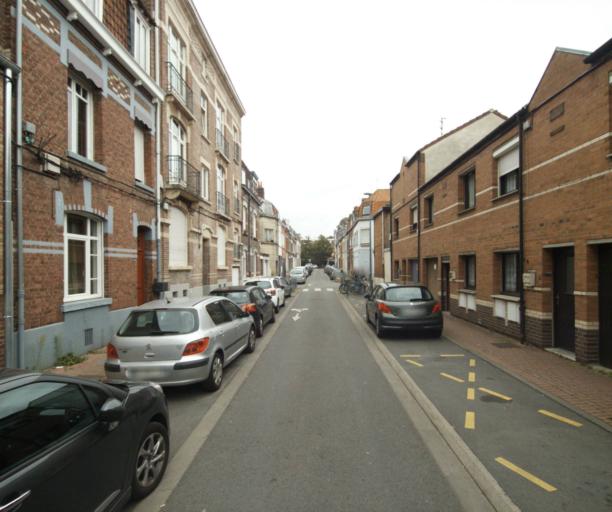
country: FR
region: Nord-Pas-de-Calais
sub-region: Departement du Nord
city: La Madeleine
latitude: 50.6364
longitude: 3.0842
